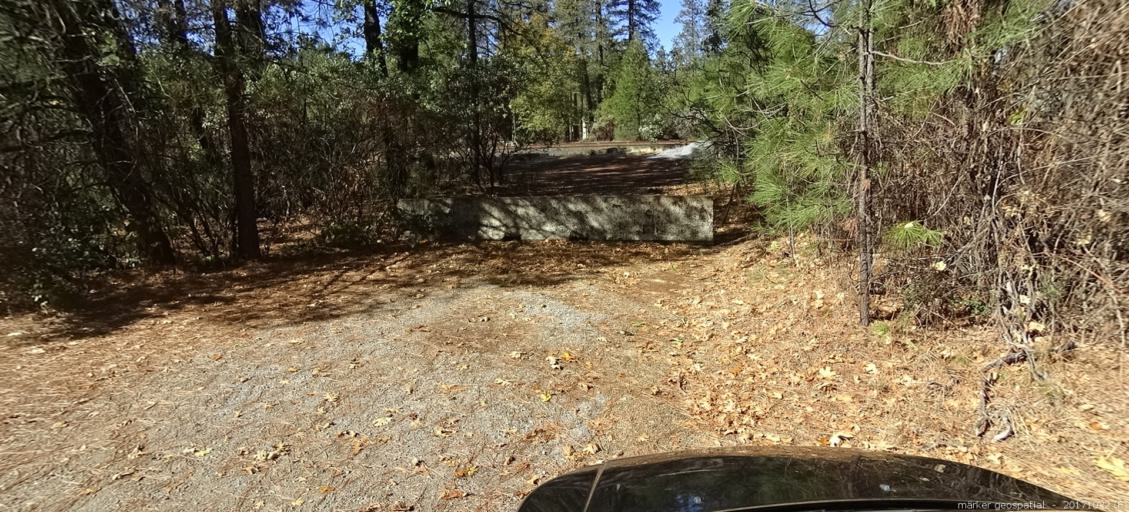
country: US
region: California
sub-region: Shasta County
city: Central Valley (historical)
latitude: 40.8873
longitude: -122.3797
